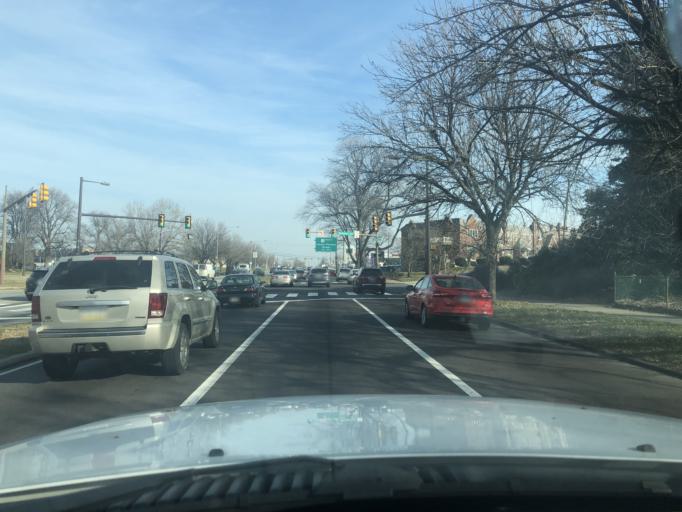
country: US
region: Pennsylvania
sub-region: Montgomery County
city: Rockledge
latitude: 40.0337
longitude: -75.0749
